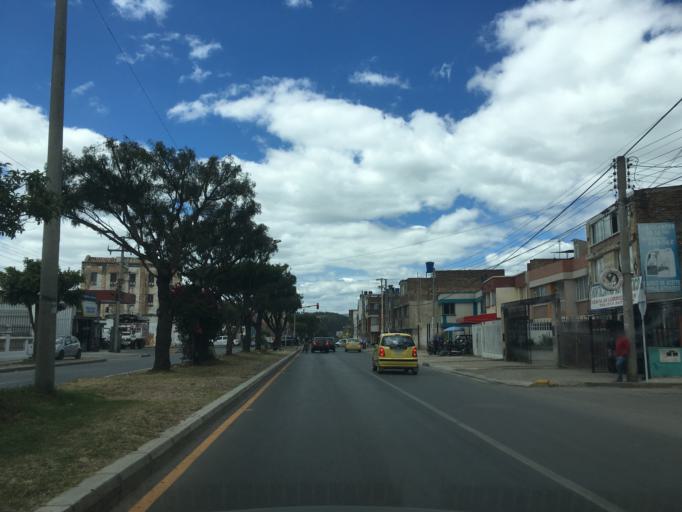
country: CO
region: Boyaca
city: Sogamoso
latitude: 5.7105
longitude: -72.9313
